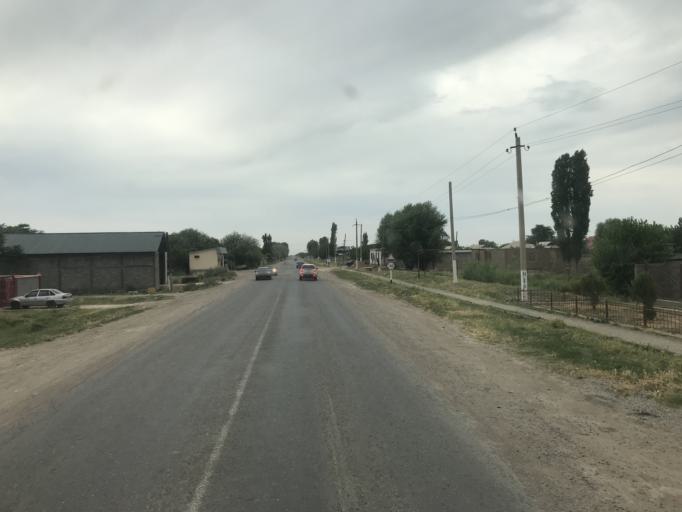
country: KZ
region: Ongtustik Qazaqstan
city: Asykata
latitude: 40.9031
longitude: 68.3567
